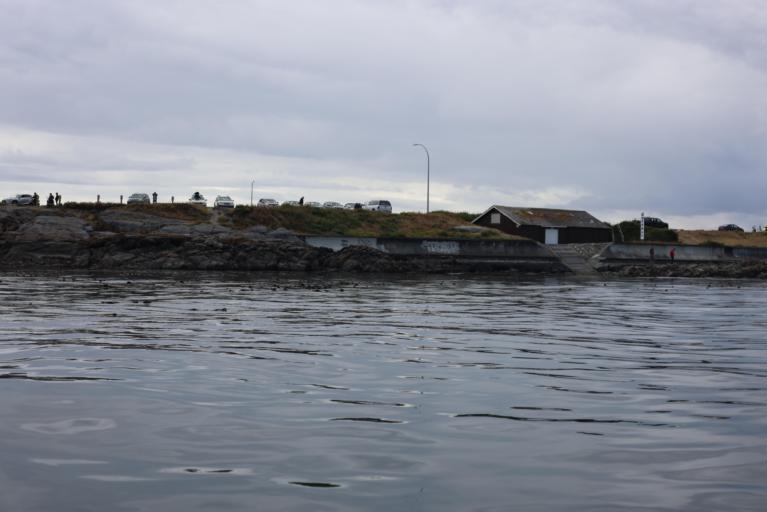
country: CA
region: British Columbia
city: Victoria
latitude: 48.4036
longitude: -123.3470
